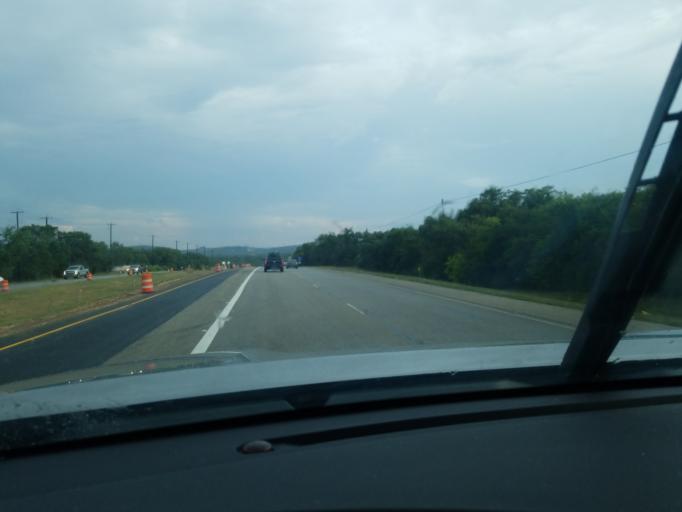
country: US
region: Texas
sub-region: Comal County
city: Bulverde
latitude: 29.7611
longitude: -98.4301
